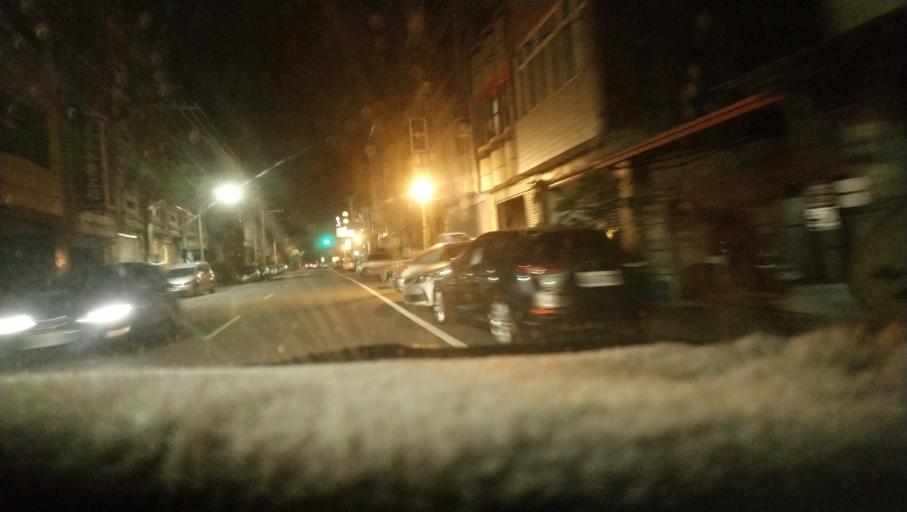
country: TW
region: Taiwan
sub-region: Yunlin
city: Douliu
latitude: 23.7091
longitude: 120.4401
